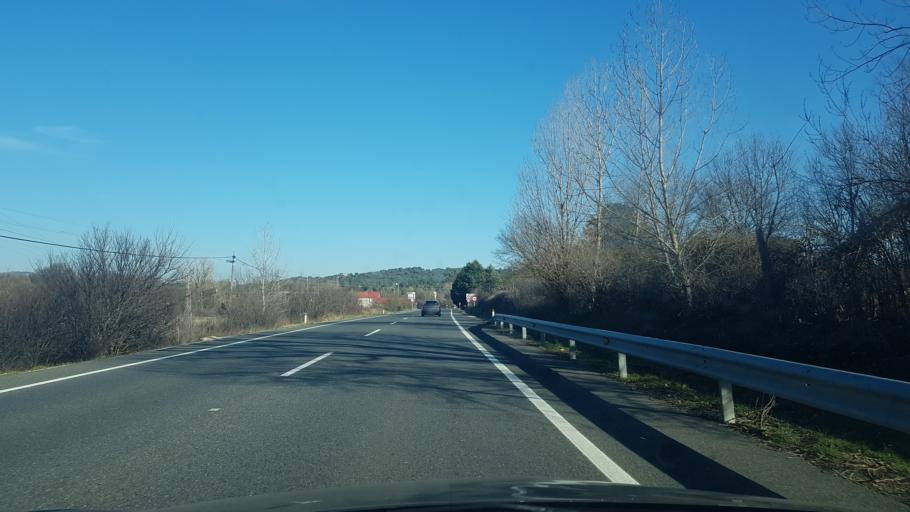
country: ES
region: Madrid
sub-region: Provincia de Madrid
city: Rozas de Puerto Real
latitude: 40.3448
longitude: -4.4486
